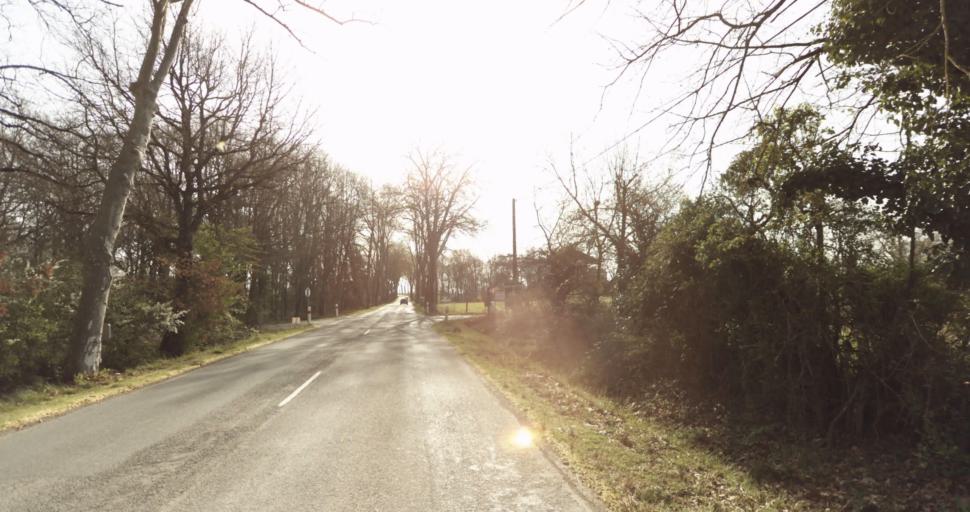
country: FR
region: Midi-Pyrenees
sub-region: Departement du Tarn
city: Saint-Sulpice-la-Pointe
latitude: 43.7606
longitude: 1.7018
